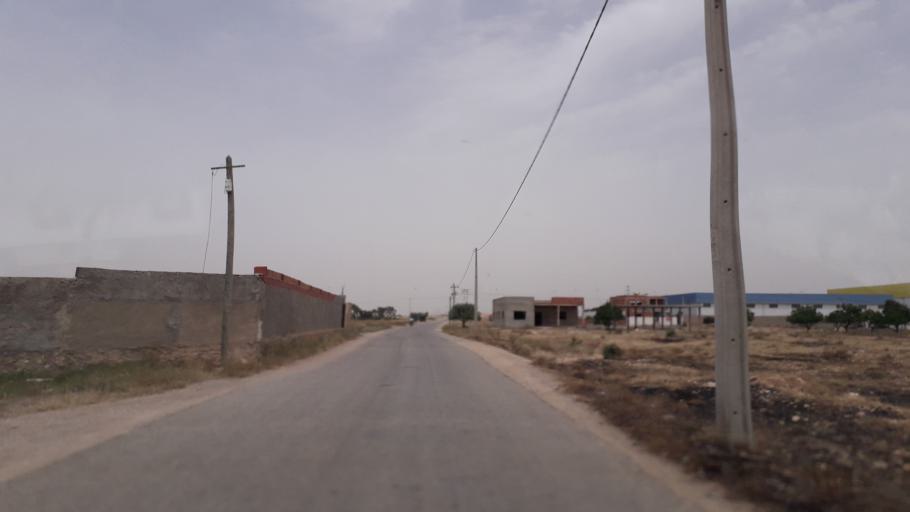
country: TN
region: Safaqis
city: Al Qarmadah
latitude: 34.8480
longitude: 10.7541
